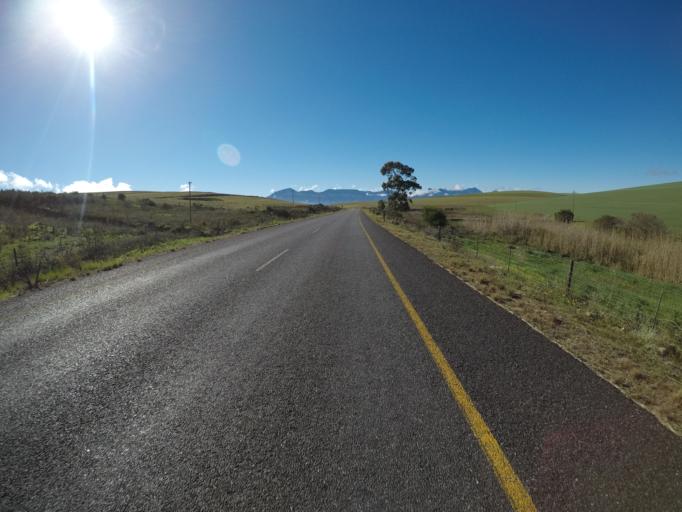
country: ZA
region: Western Cape
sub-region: Overberg District Municipality
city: Caledon
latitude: -34.1345
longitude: 19.5098
